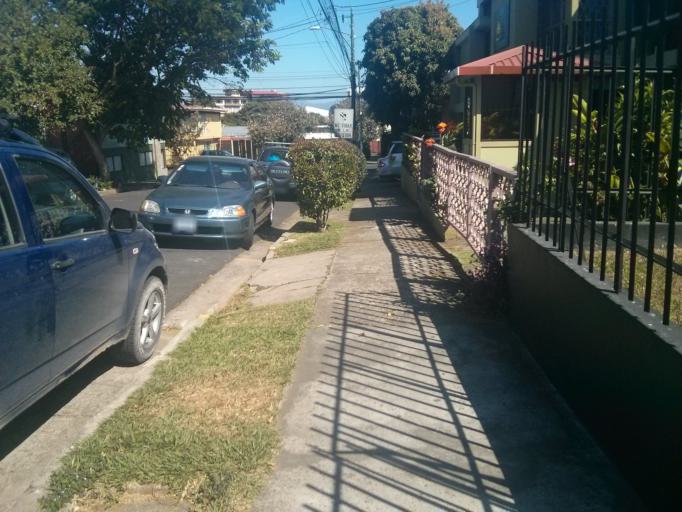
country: CR
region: San Jose
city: San Pedro
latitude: 9.9288
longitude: -84.0467
